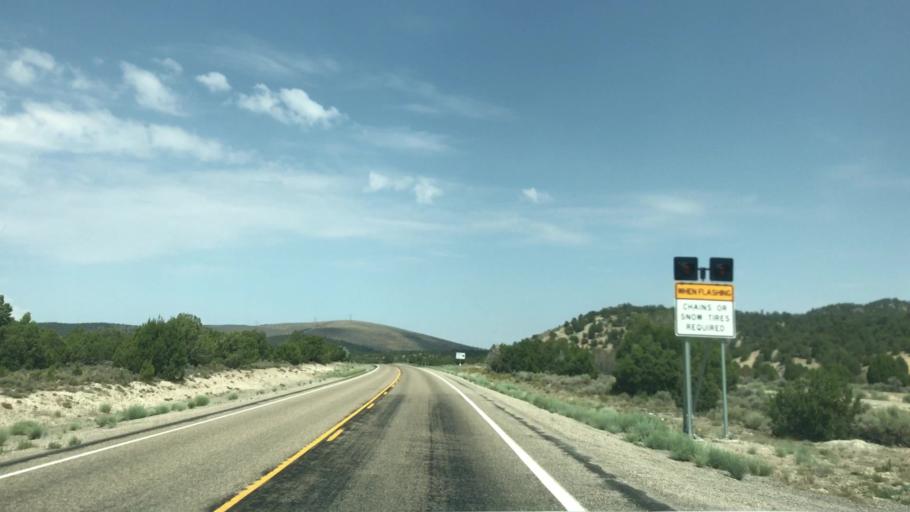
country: US
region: Nevada
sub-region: White Pine County
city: Ely
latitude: 39.3805
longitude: -115.0661
